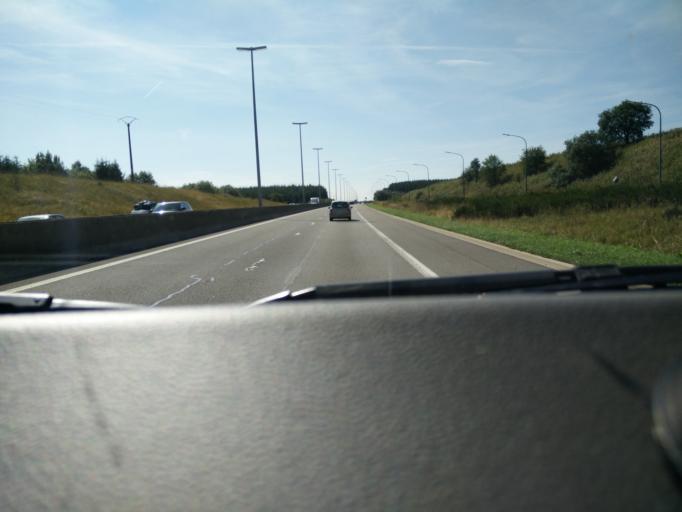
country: BE
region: Wallonia
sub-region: Province du Luxembourg
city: Leglise
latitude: 49.8531
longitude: 5.5104
